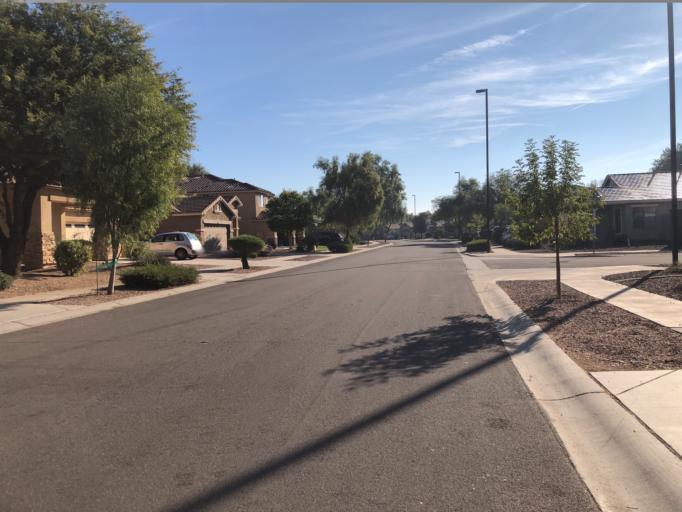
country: US
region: Arizona
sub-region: Maricopa County
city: Queen Creek
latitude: 33.2774
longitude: -111.6917
